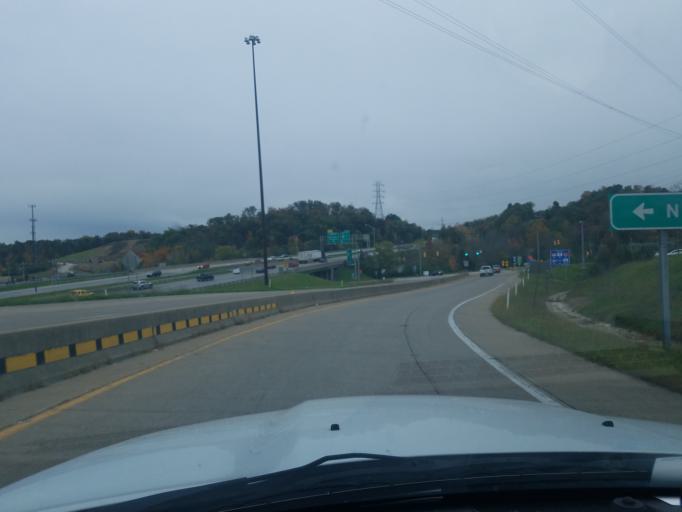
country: US
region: Indiana
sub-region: Floyd County
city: New Albany
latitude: 38.3126
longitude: -85.8453
